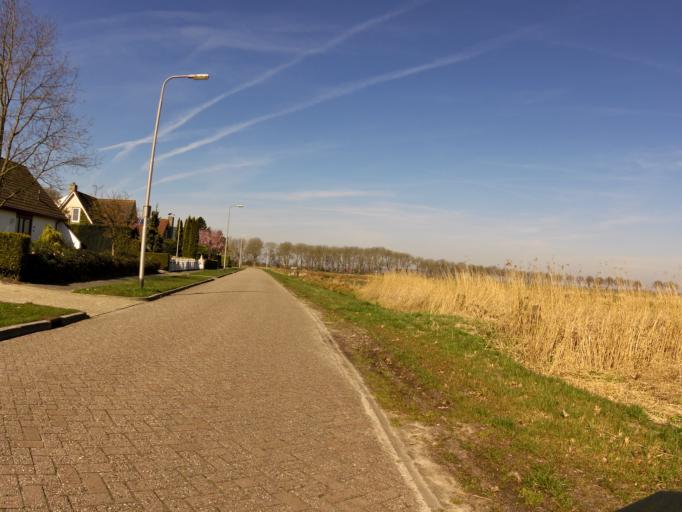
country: NL
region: Overijssel
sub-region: Gemeente Steenwijkerland
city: Oldemarkt
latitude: 52.8081
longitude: 5.9244
